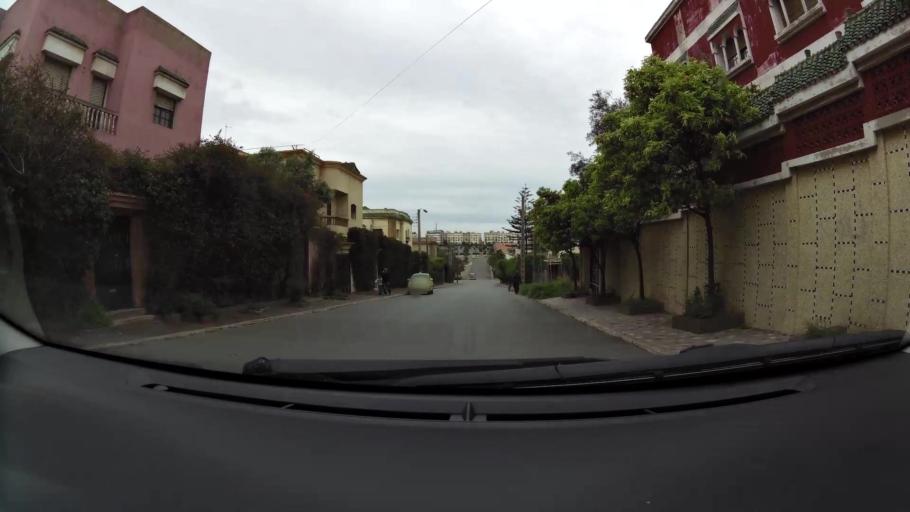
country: MA
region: Grand Casablanca
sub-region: Mediouna
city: Tit Mellil
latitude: 33.5639
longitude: -7.5360
